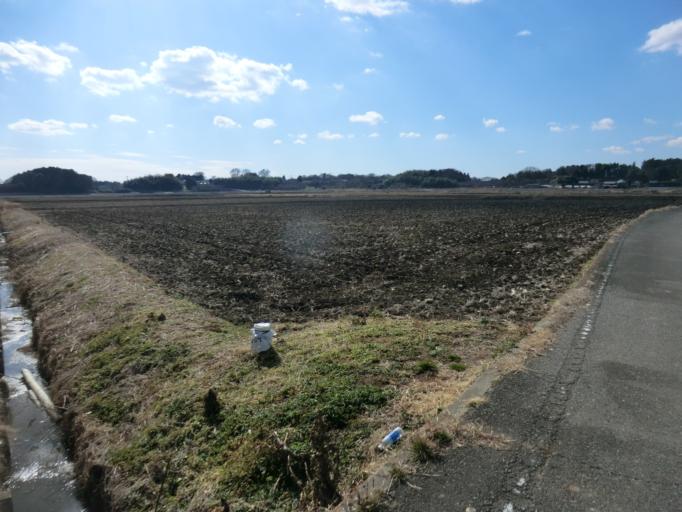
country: JP
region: Ibaraki
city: Naka
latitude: 36.0987
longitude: 140.1379
